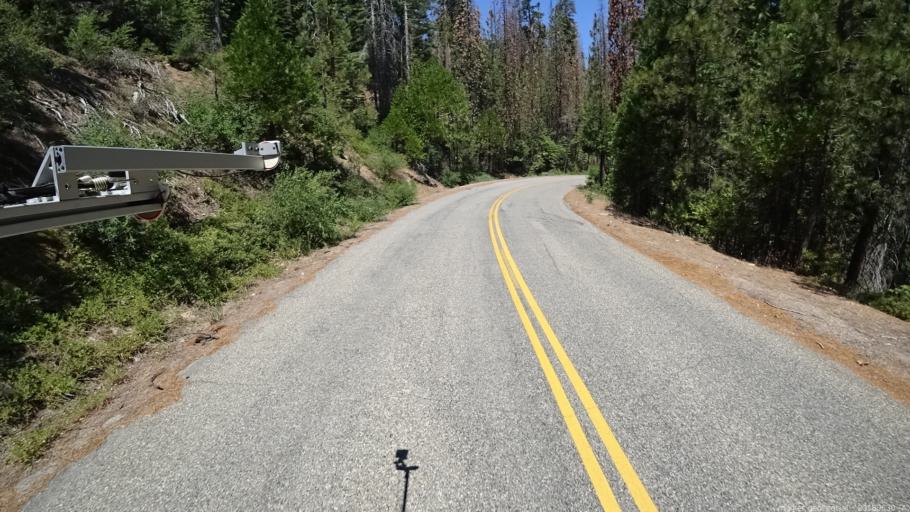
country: US
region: California
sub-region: Madera County
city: Oakhurst
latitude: 37.3545
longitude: -119.3864
